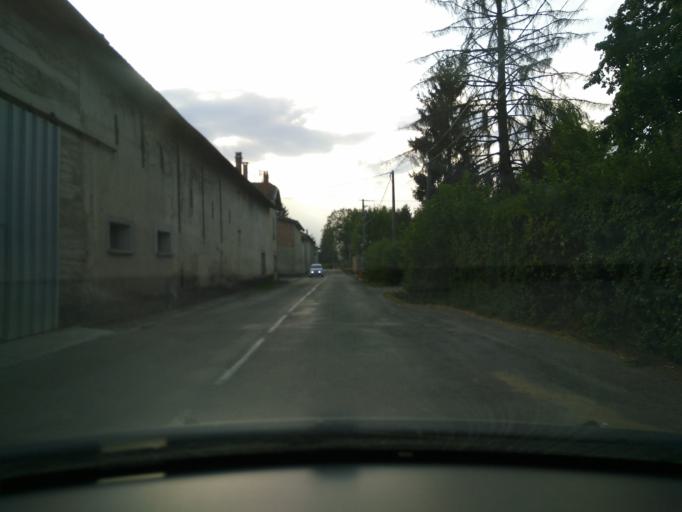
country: FR
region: Rhone-Alpes
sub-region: Departement de l'Isere
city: Viriville
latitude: 45.3944
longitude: 5.1633
